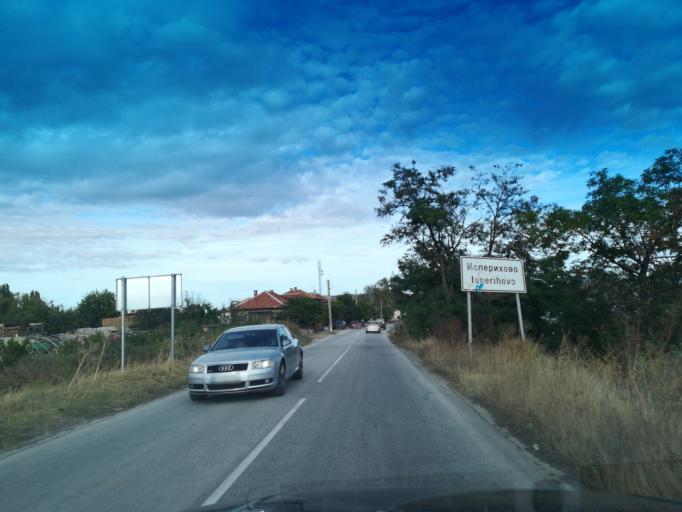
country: BG
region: Plovdiv
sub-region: Obshtina Krichim
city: Krichim
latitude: 42.0817
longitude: 24.4216
